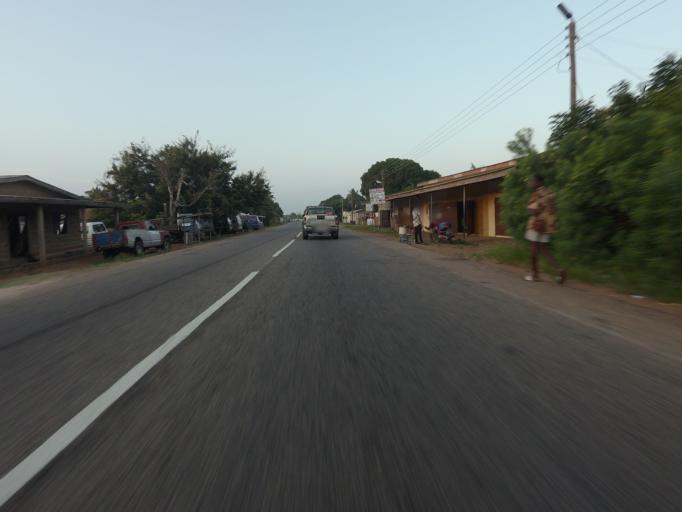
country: GH
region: Volta
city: Anloga
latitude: 5.8246
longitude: 0.9483
